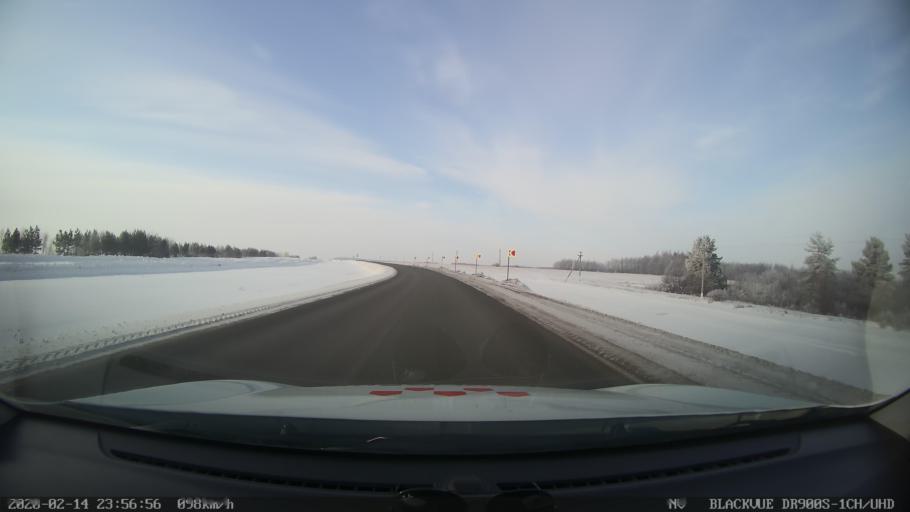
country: RU
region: Tatarstan
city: Kuybyshevskiy Zaton
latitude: 55.3302
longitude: 49.1207
